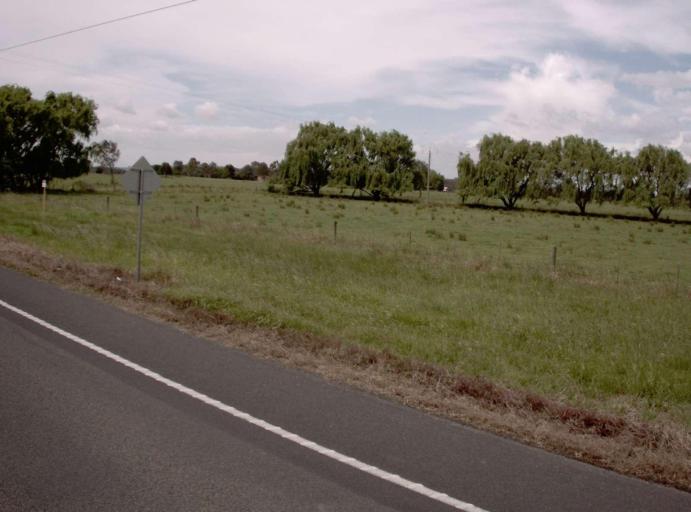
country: AU
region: Victoria
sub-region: Wellington
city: Sale
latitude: -38.0667
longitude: 147.0318
